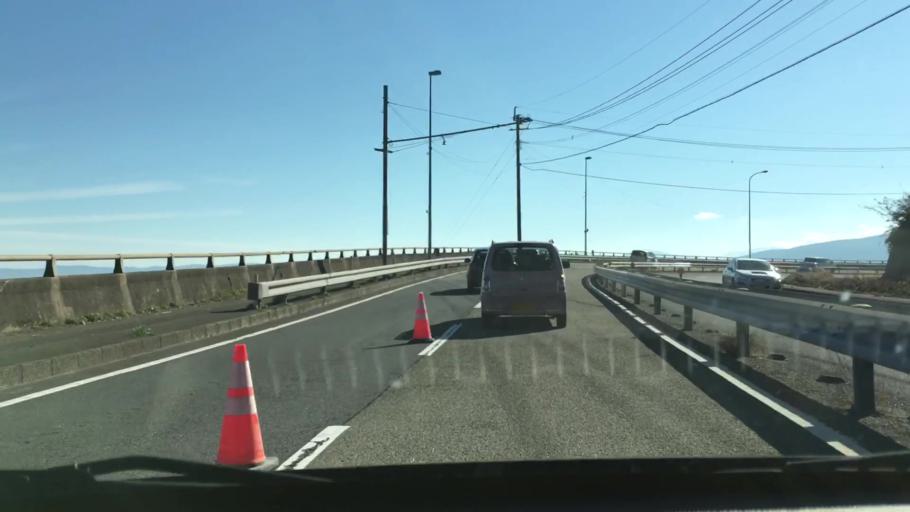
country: JP
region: Kagoshima
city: Kajiki
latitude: 31.6592
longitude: 130.6185
